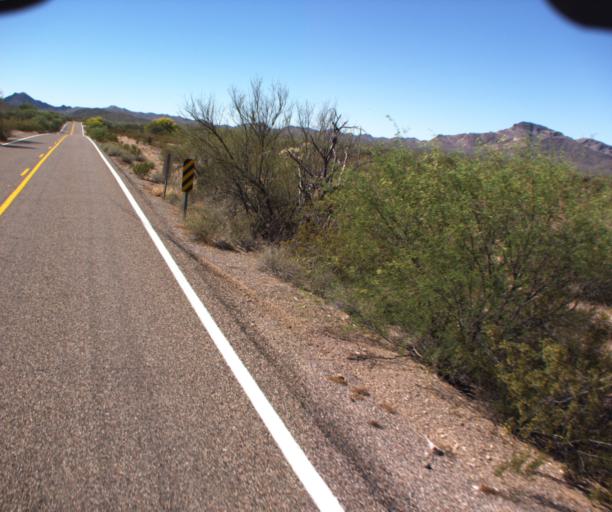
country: MX
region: Sonora
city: Sonoyta
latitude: 32.0352
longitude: -112.7974
